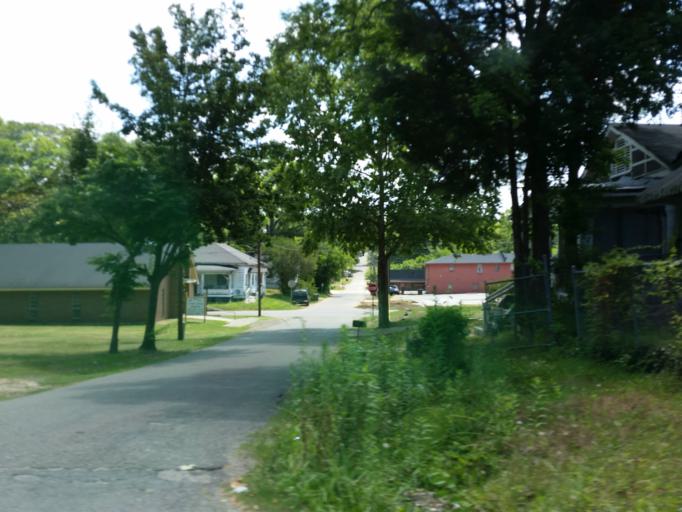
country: US
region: Mississippi
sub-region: Lauderdale County
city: Meridian
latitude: 32.3697
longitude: -88.7137
